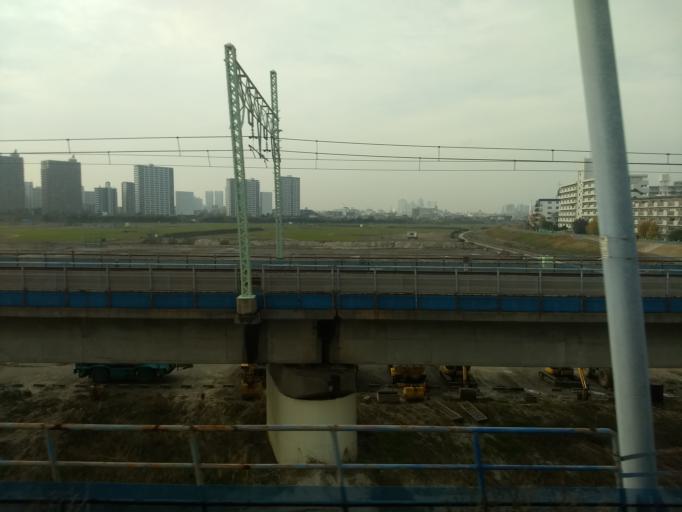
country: JP
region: Kanagawa
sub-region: Kawasaki-shi
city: Kawasaki
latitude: 35.5394
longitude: 139.7054
